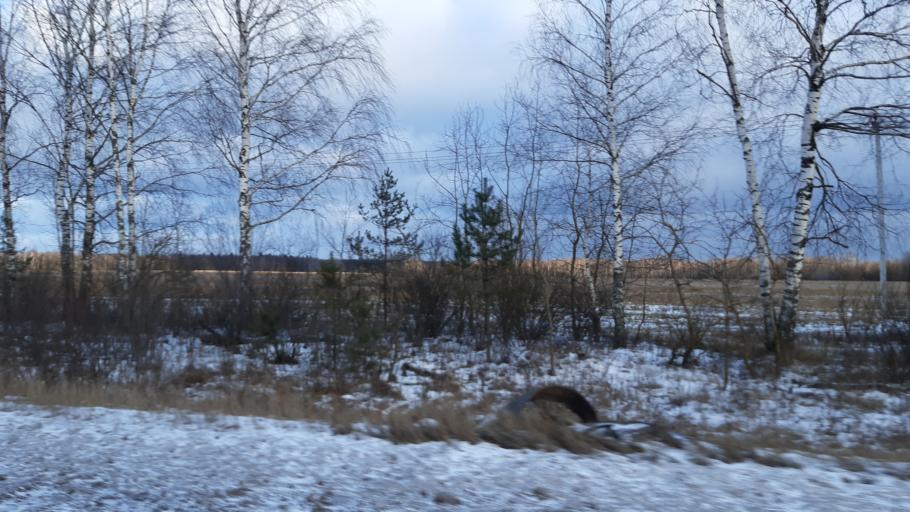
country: RU
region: Moskovskaya
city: Noginsk-9
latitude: 56.0245
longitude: 38.5561
